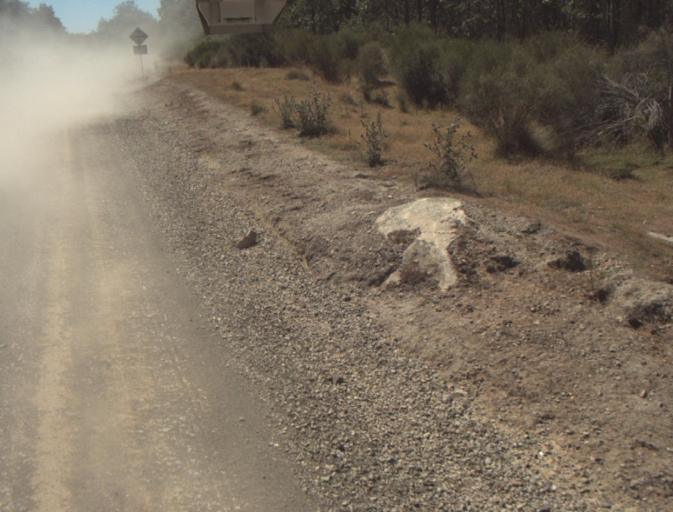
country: AU
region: Tasmania
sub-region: Dorset
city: Scottsdale
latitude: -41.3120
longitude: 147.4660
